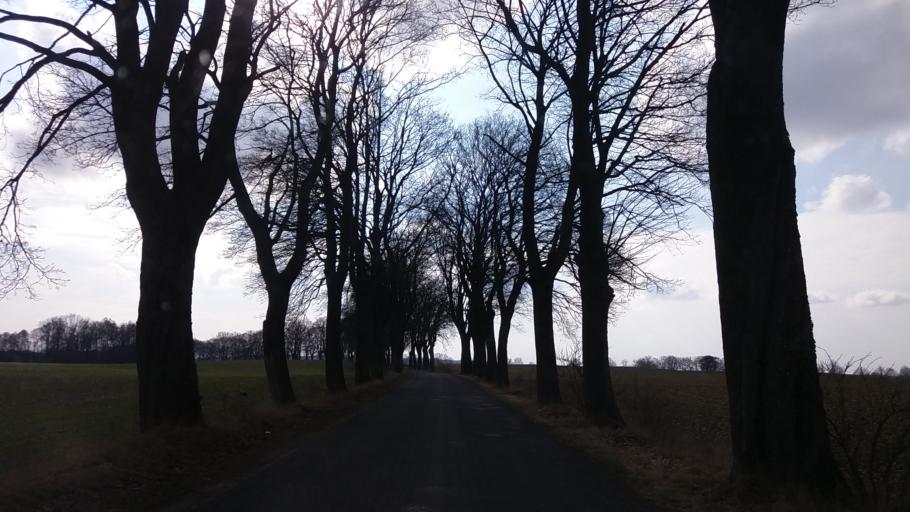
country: PL
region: West Pomeranian Voivodeship
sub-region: Powiat choszczenski
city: Recz
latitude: 53.1702
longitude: 15.6101
